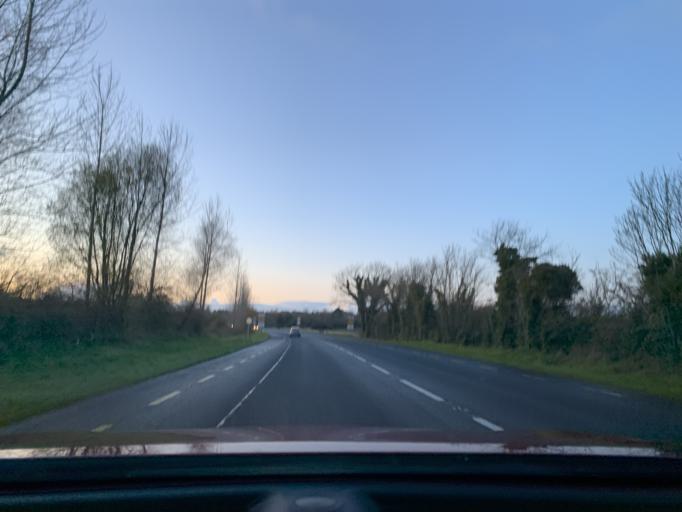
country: IE
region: Connaught
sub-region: County Leitrim
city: Carrick-on-Shannon
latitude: 53.9162
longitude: -7.9762
